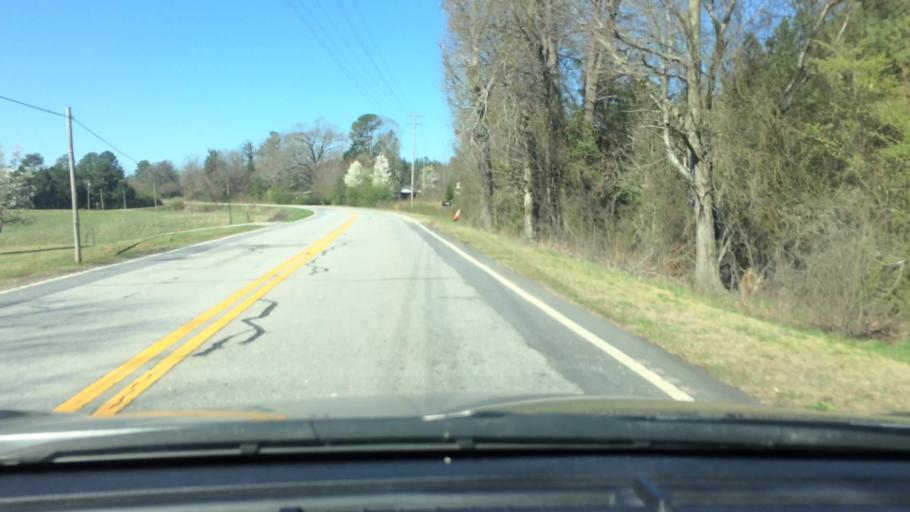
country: US
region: South Carolina
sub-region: Oconee County
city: Utica
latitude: 34.7132
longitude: -82.9043
